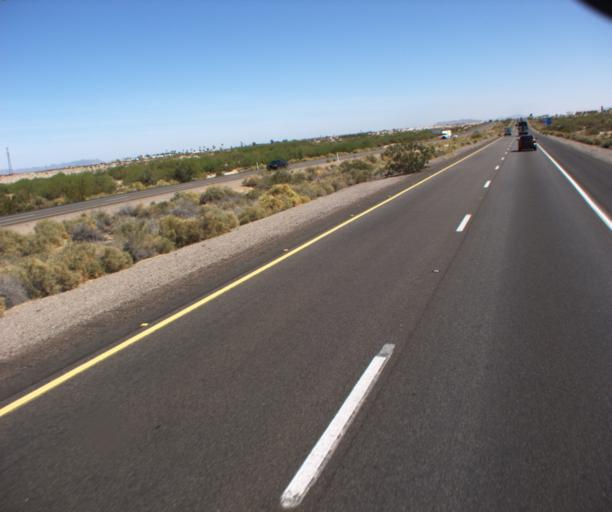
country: US
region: Arizona
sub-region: Yuma County
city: Wellton
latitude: 32.6565
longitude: -114.1644
